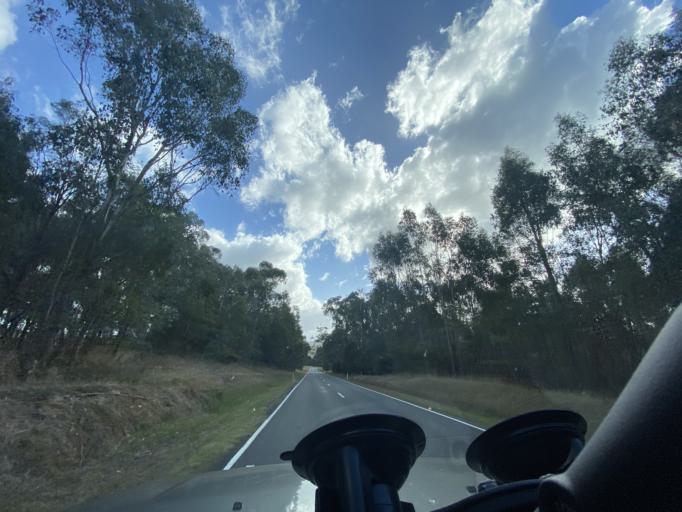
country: AU
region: Victoria
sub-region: Murrindindi
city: Kinglake West
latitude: -37.3224
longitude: 145.3067
